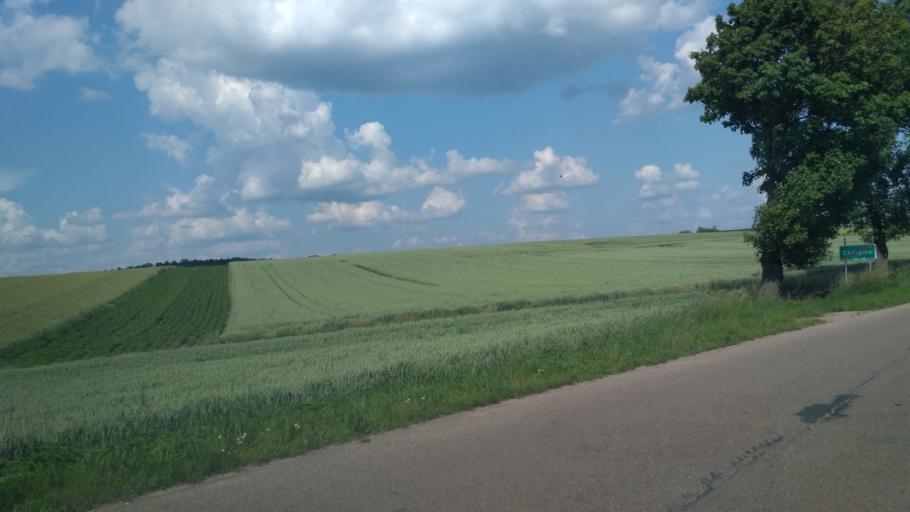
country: PL
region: Subcarpathian Voivodeship
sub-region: Powiat jaroslawski
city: Pawlosiow
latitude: 49.9451
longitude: 22.6879
